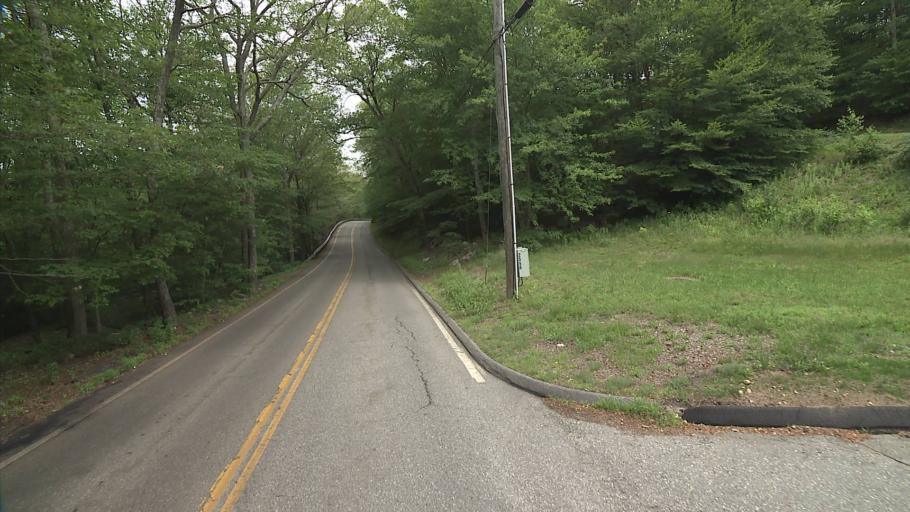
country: US
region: Connecticut
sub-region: New London County
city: Ledyard Center
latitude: 41.4577
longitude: -71.9617
